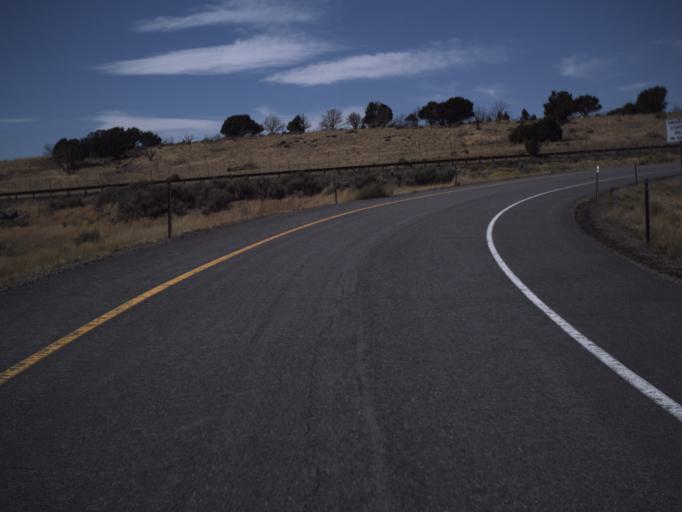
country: US
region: Utah
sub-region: Beaver County
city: Beaver
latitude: 38.5790
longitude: -112.6019
